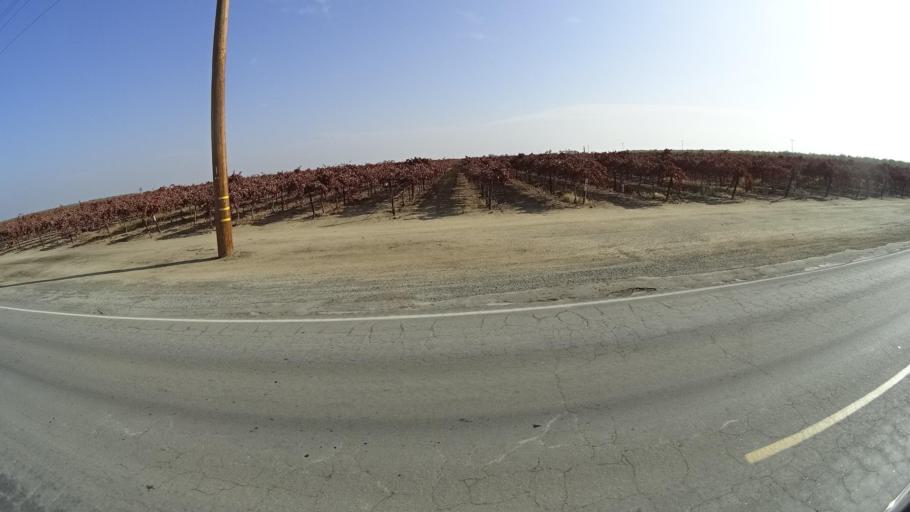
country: US
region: California
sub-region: Kern County
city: Delano
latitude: 35.7411
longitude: -119.2232
